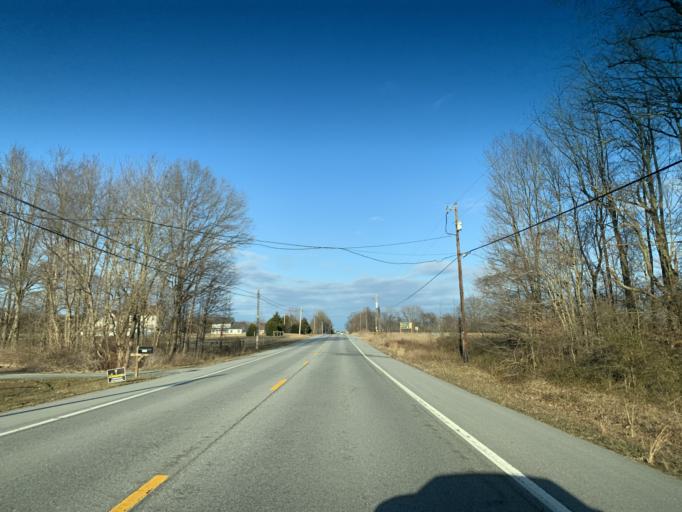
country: US
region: Maryland
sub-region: Queen Anne's County
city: Kingstown
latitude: 39.1684
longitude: -75.9277
